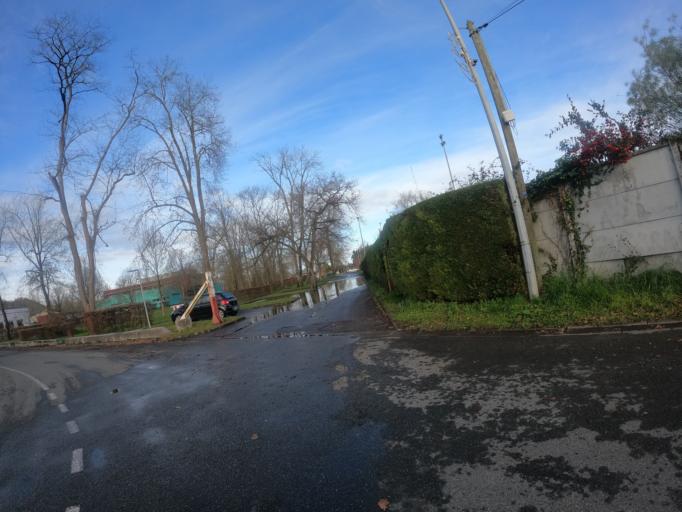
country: FR
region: Aquitaine
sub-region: Departement des Pyrenees-Atlantiques
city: Billere
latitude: 43.2926
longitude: -0.4013
